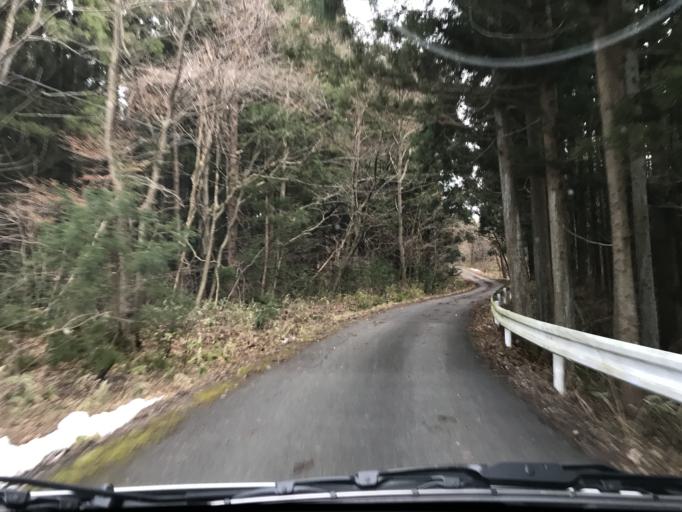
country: JP
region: Iwate
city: Ichinoseki
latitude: 38.9772
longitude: 141.0398
